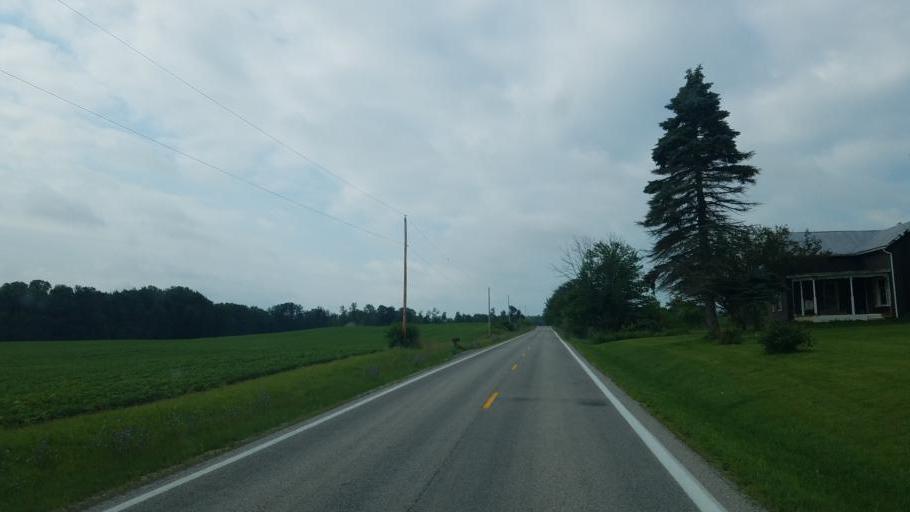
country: US
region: Ohio
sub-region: Knox County
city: Centerburg
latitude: 40.3834
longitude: -82.6965
